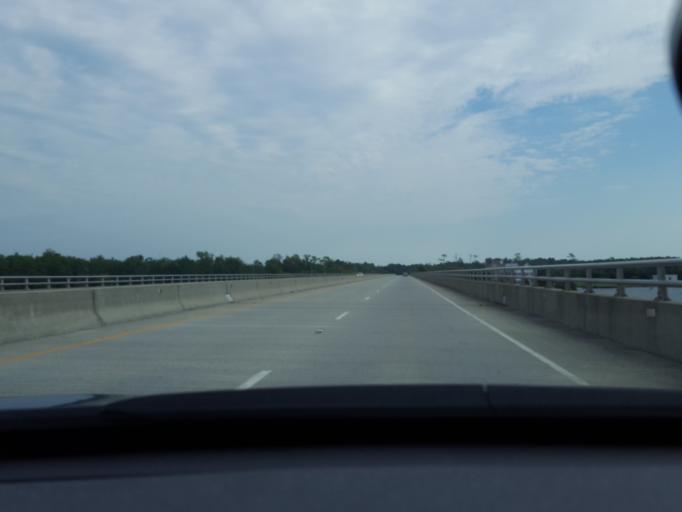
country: US
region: North Carolina
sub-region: Chowan County
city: Edenton
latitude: 36.0520
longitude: -76.6863
